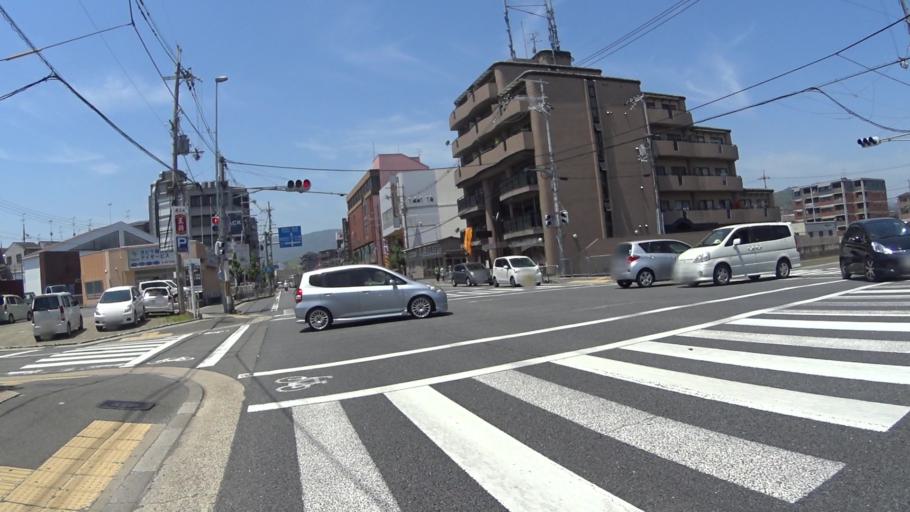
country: JP
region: Kyoto
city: Muko
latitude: 34.9924
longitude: 135.7060
